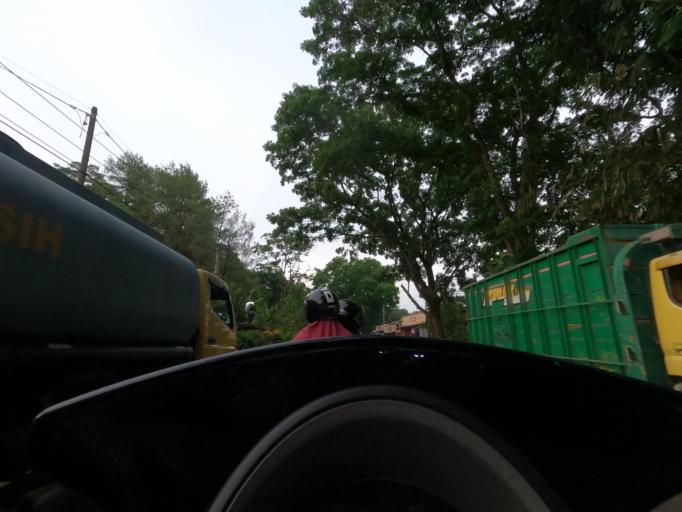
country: ID
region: West Java
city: Lembang
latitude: -6.5852
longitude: 107.7415
